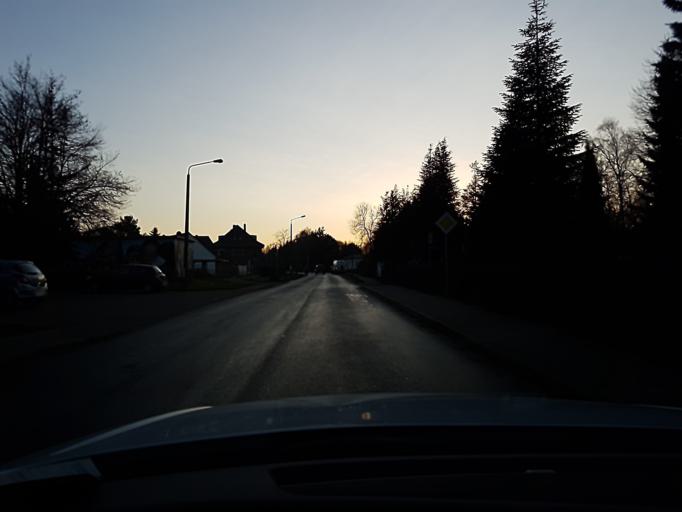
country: DE
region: Mecklenburg-Vorpommern
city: Wiek
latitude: 54.6188
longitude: 13.2878
